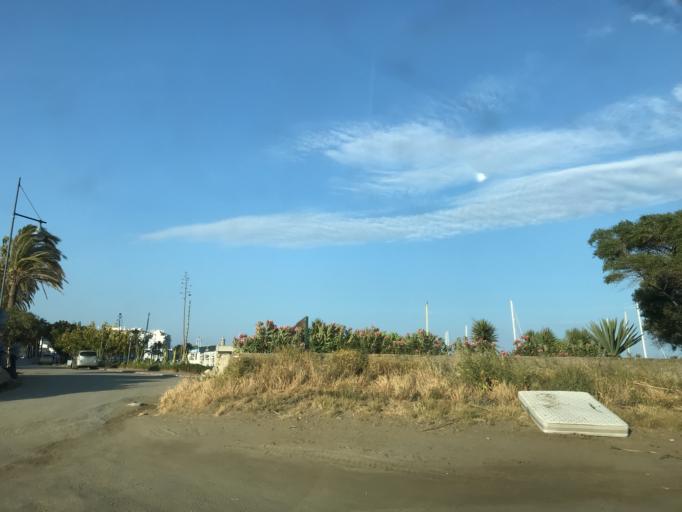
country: ES
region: Andalusia
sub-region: Provincia de Malaga
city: Estepona
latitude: 36.4141
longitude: -5.1607
